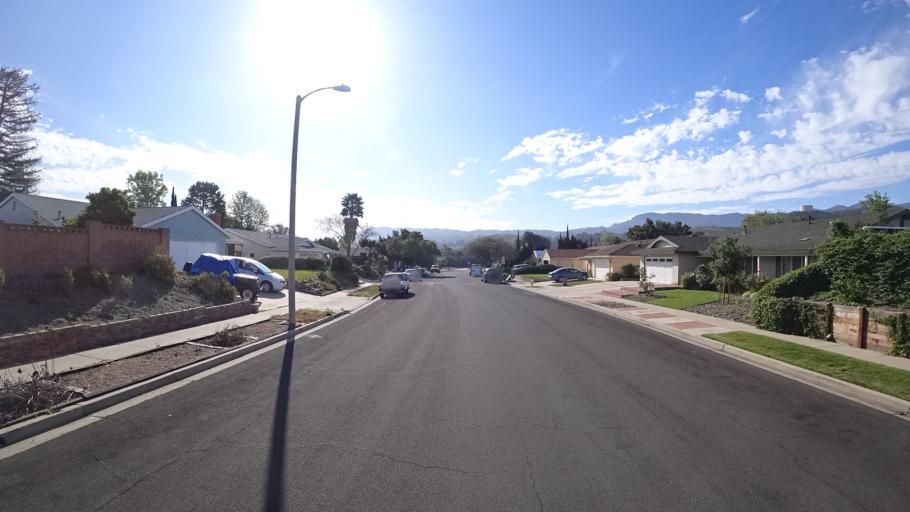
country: US
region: California
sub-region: Ventura County
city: Casa Conejo
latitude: 34.1754
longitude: -118.9522
